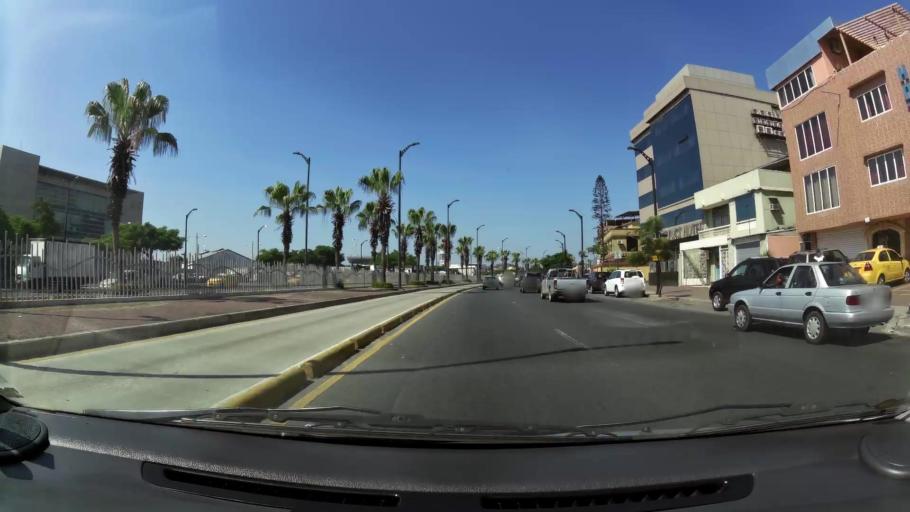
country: EC
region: Guayas
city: Eloy Alfaro
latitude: -2.1525
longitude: -79.8862
